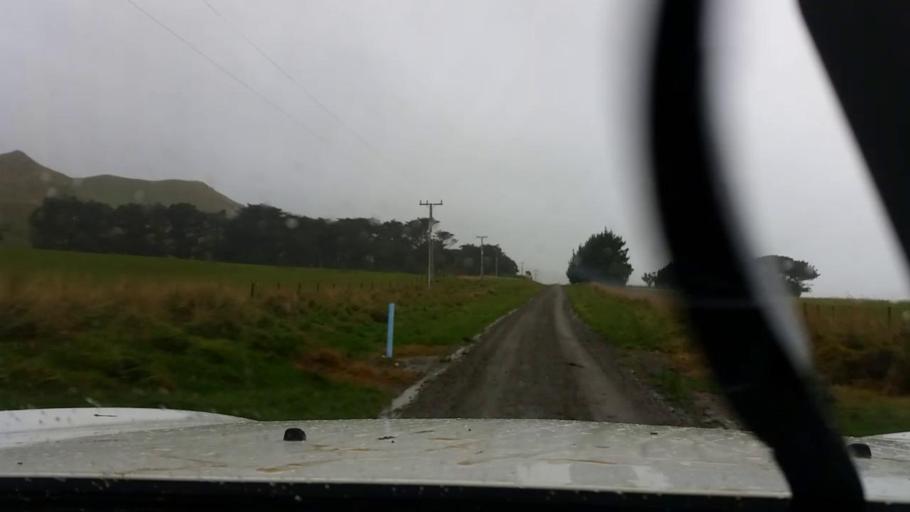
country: NZ
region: Wellington
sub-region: Masterton District
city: Masterton
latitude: -41.2590
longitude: 175.9002
